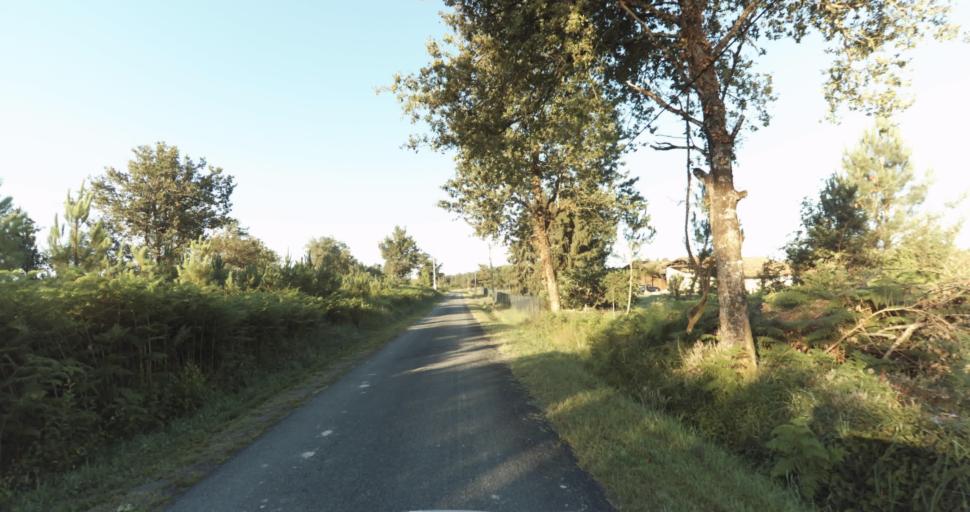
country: FR
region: Aquitaine
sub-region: Departement de la Gironde
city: Bazas
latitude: 44.4089
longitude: -0.2450
